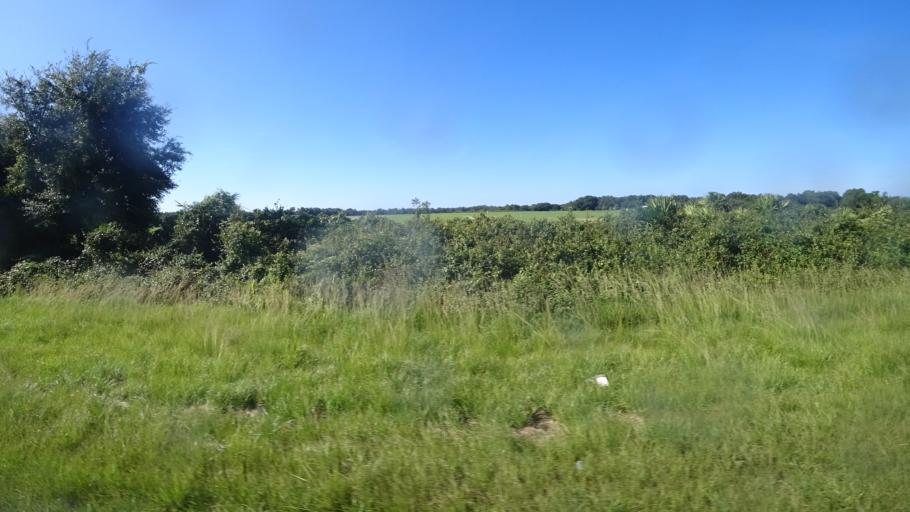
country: US
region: Florida
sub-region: Hillsborough County
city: Sun City Center
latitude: 27.6643
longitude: -82.3332
